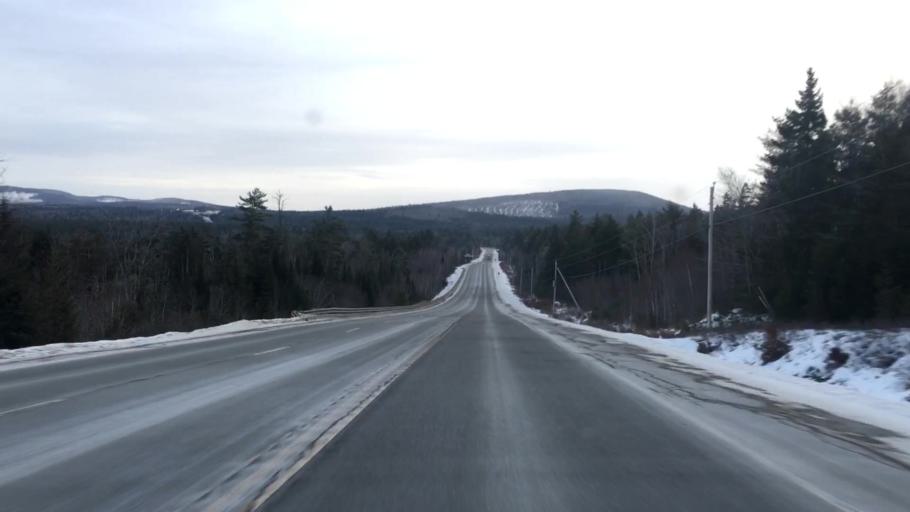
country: US
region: Maine
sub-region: Hancock County
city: Franklin
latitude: 44.8256
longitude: -68.1008
